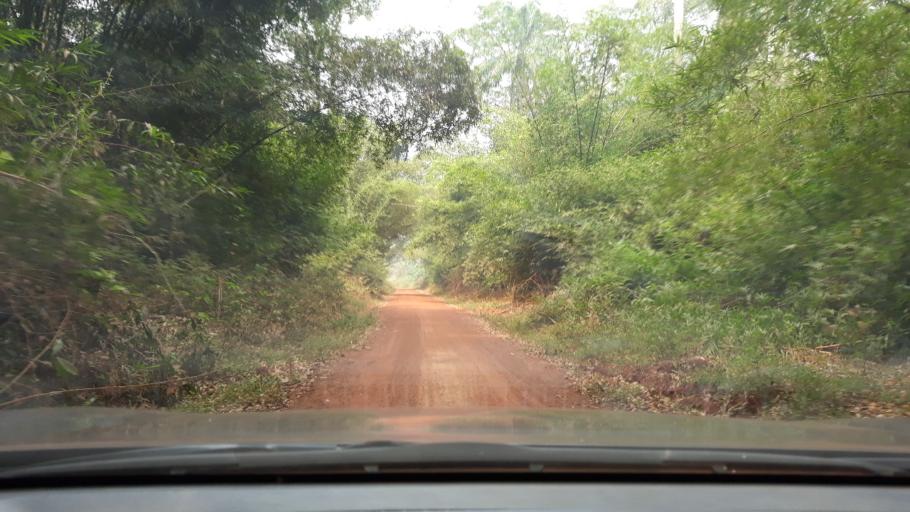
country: CD
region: Eastern Province
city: Aketi
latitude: 2.9175
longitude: 24.0626
